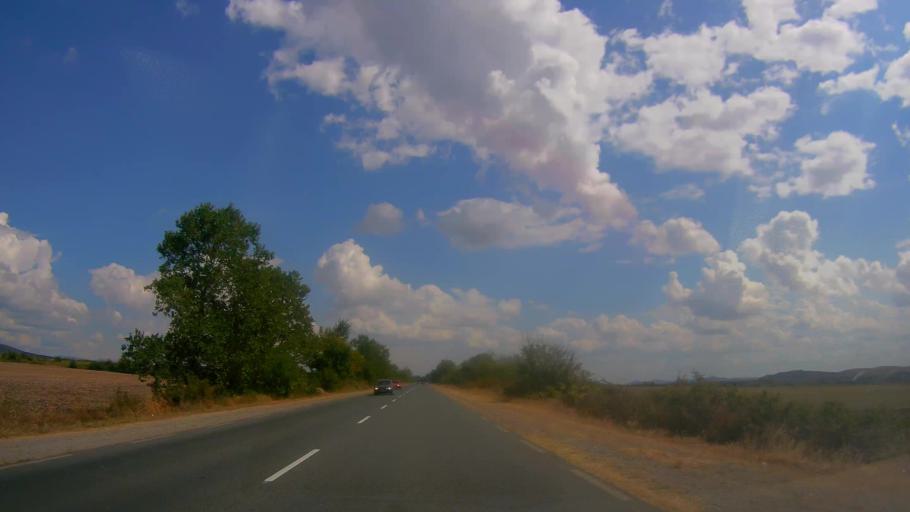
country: BG
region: Sliven
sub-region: Obshtina Sliven
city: Kermen
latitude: 42.6339
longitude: 26.1646
